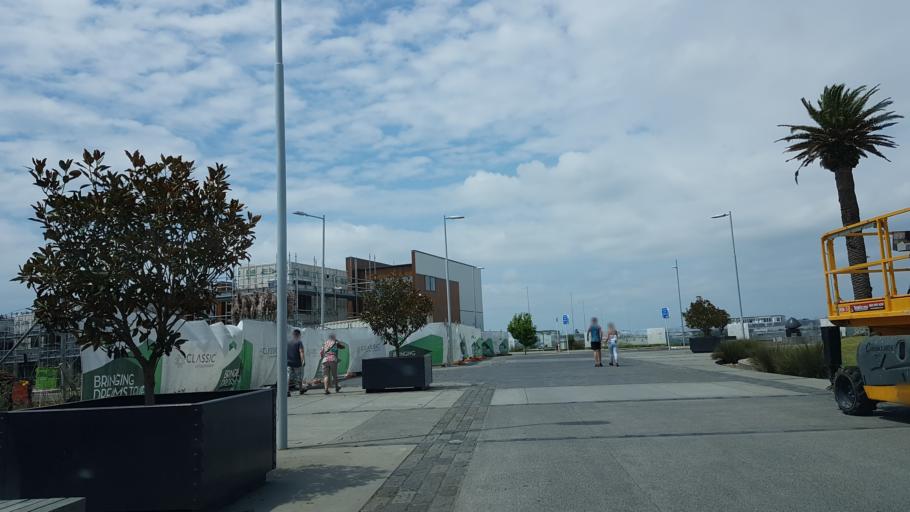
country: NZ
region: Auckland
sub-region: Auckland
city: North Shore
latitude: -36.7878
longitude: 174.6662
